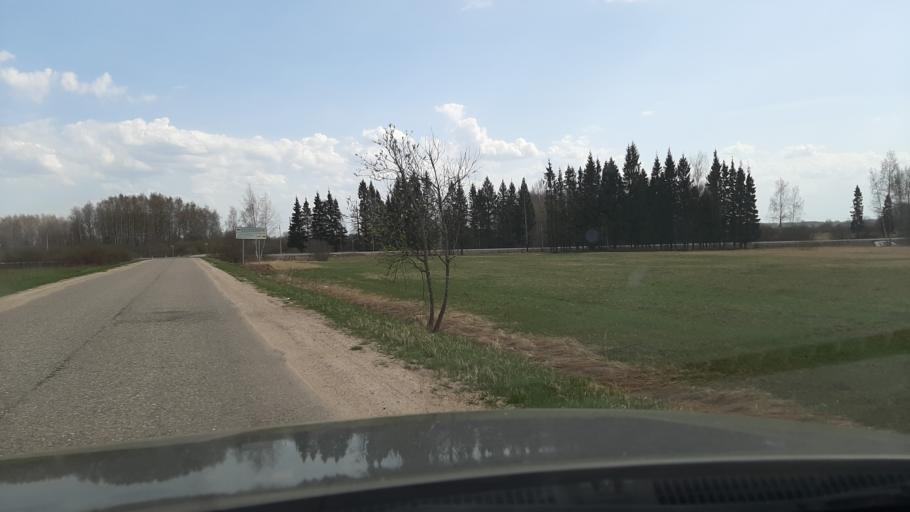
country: RU
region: Ivanovo
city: Furmanov
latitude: 57.2946
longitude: 41.1766
